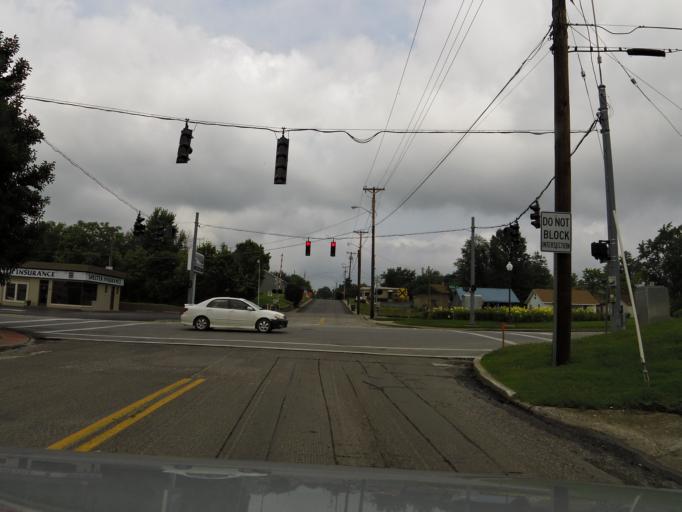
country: US
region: Kentucky
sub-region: Hopkins County
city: Madisonville
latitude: 37.3355
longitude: -87.4974
